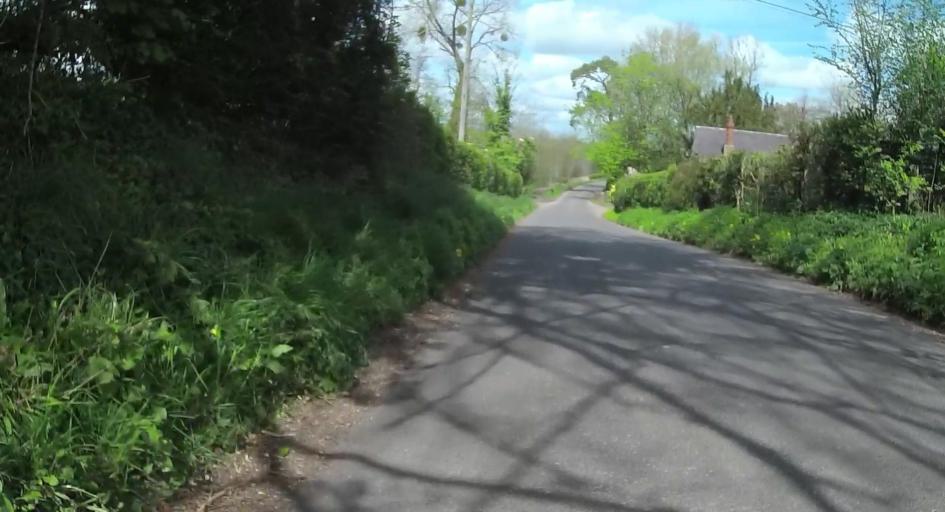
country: GB
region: England
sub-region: Hampshire
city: Romsey
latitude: 51.0797
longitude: -1.5237
